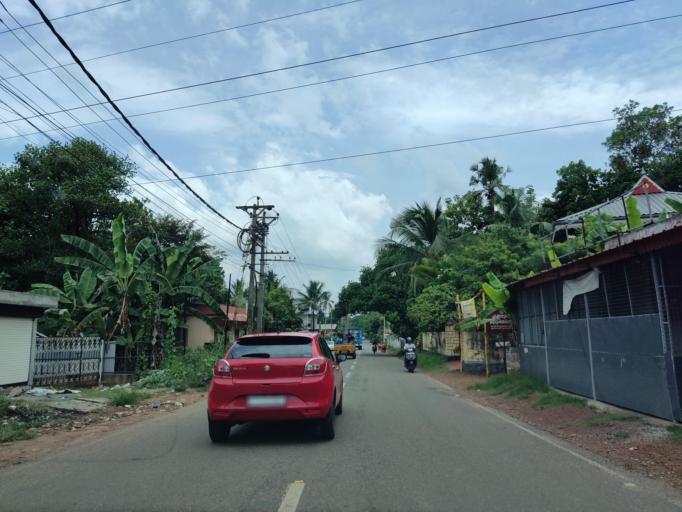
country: IN
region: Kerala
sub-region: Alappuzha
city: Mavelikara
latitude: 9.2280
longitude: 76.6256
